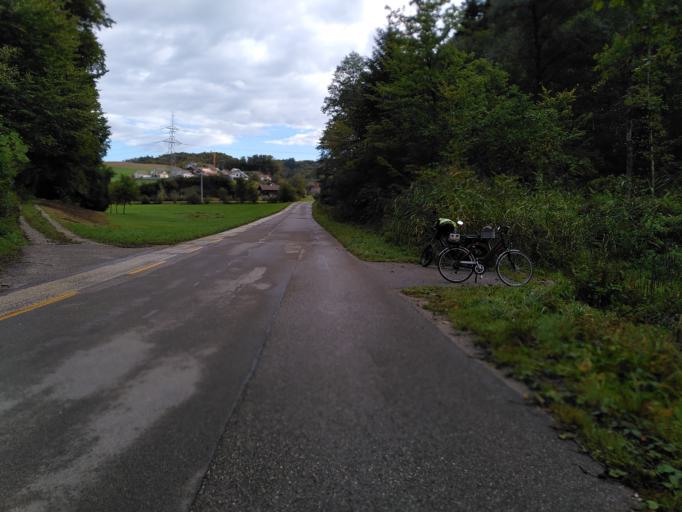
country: CH
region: Bern
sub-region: Emmental District
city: Wynigen
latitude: 47.1046
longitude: 7.6540
